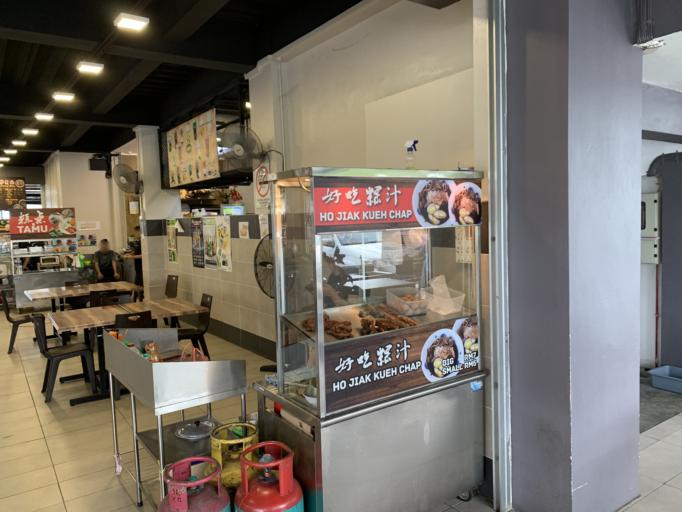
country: MY
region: Sarawak
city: Simanggang
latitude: 1.2387
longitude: 111.4569
